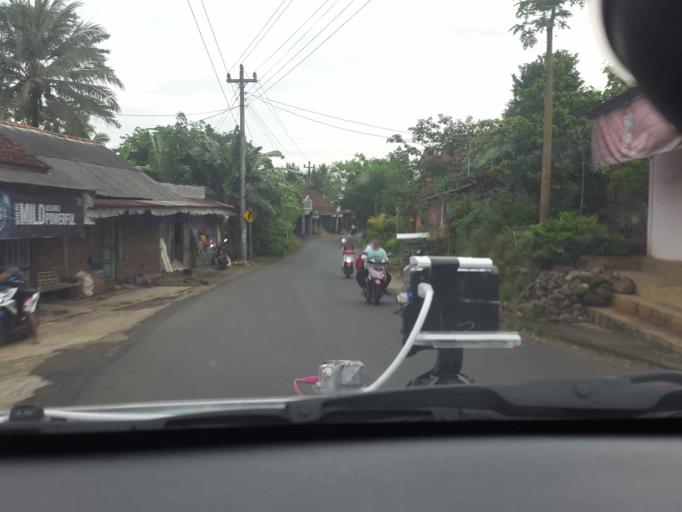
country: ID
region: Central Java
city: Banyumas
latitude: -7.5323
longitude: 109.3124
